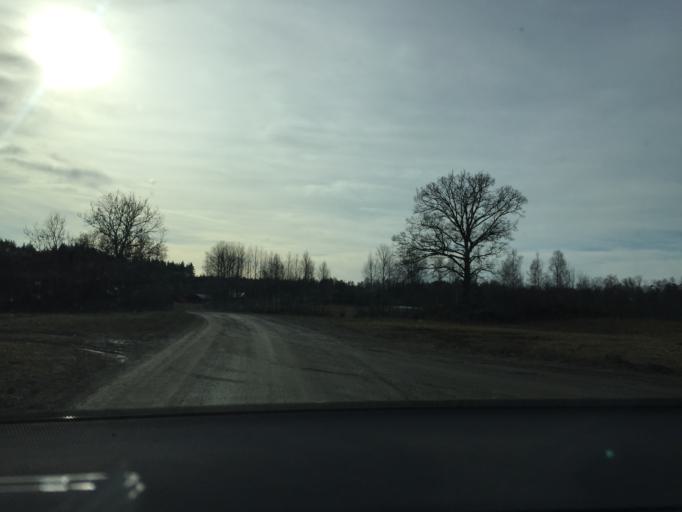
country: SE
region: OErebro
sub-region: Orebro Kommun
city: Odensbacken
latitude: 59.1266
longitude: 15.4737
